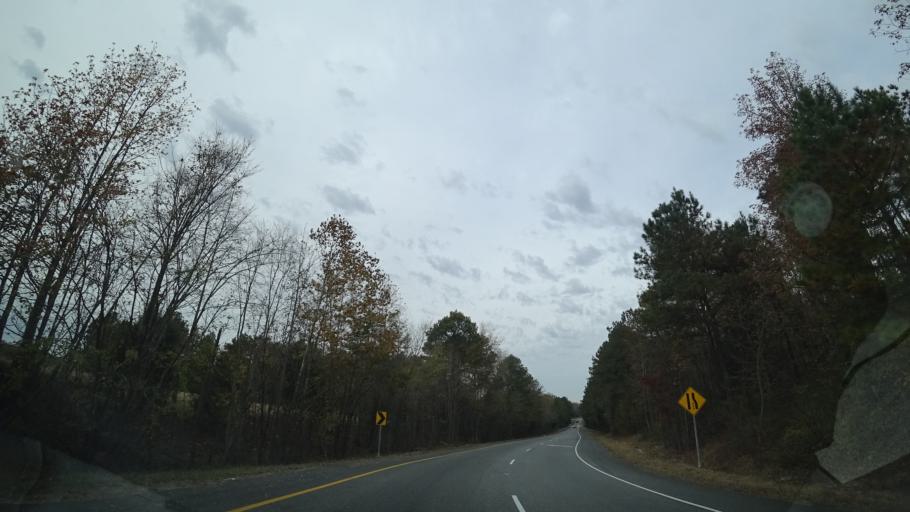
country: US
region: Virginia
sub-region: Hanover County
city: Mechanicsville
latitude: 37.6088
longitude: -77.3577
